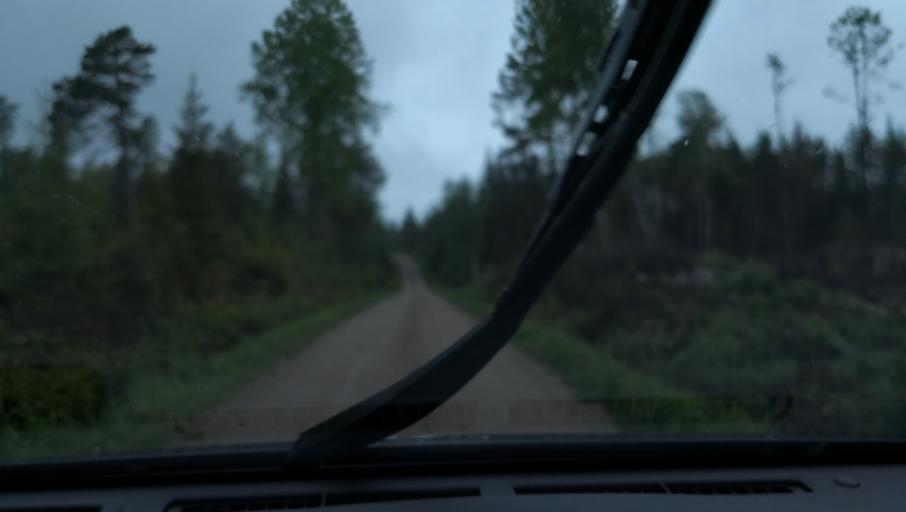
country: SE
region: Uppsala
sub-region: Enkopings Kommun
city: Orsundsbro
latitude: 59.9314
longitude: 17.3286
